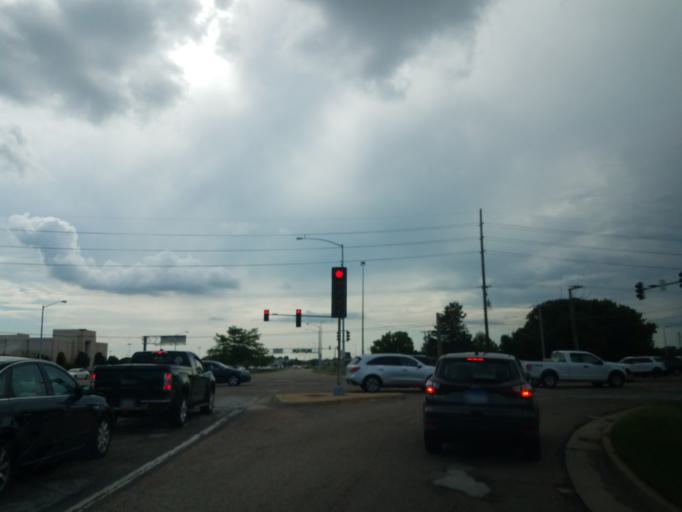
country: US
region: Illinois
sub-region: McLean County
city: Bloomington
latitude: 40.4884
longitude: -88.9524
